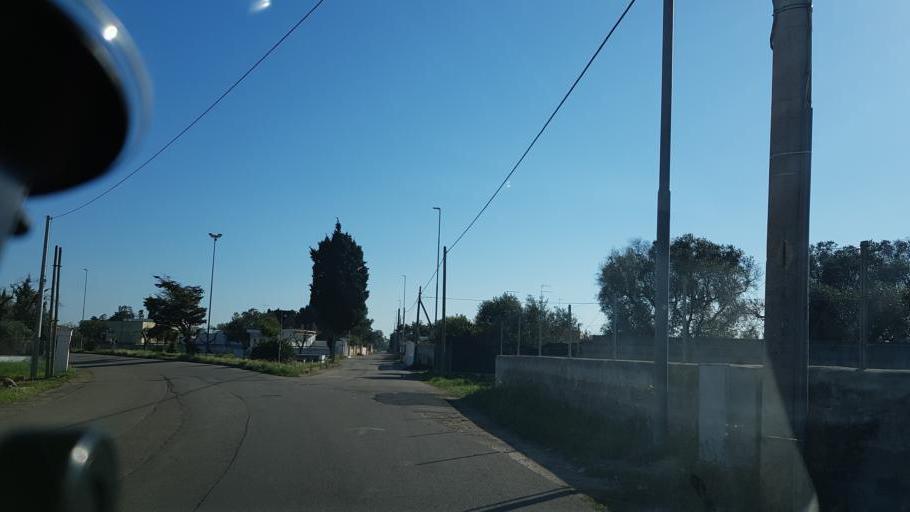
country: IT
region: Apulia
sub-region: Provincia di Brindisi
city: Torchiarolo
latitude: 40.4928
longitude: 18.1190
